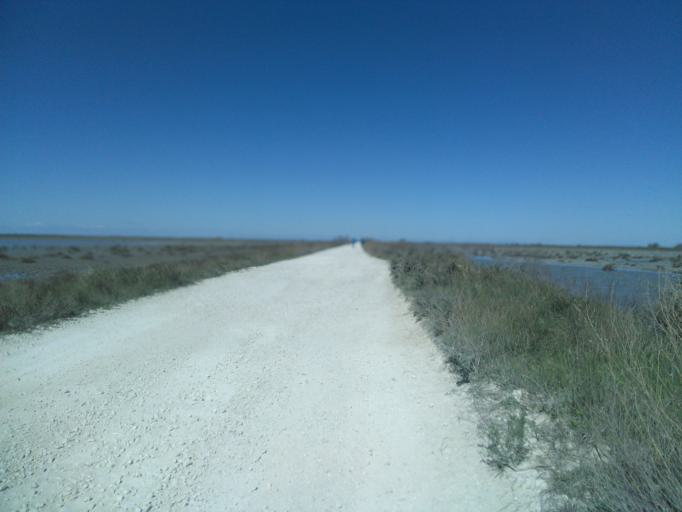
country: FR
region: Provence-Alpes-Cote d'Azur
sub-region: Departement des Bouches-du-Rhone
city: Saintes-Maries-de-la-Mer
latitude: 43.4489
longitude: 4.5971
